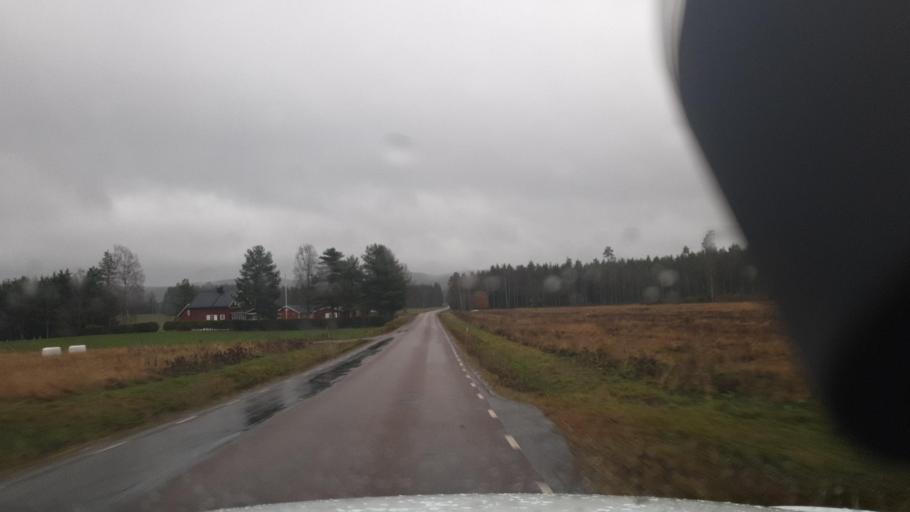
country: SE
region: Vaermland
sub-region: Eda Kommun
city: Charlottenberg
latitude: 59.7414
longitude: 12.1674
